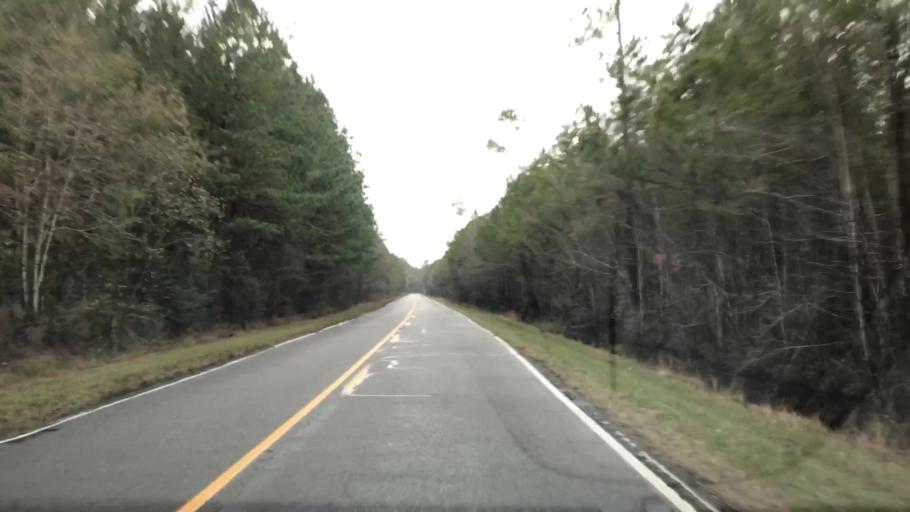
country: US
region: South Carolina
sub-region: Georgetown County
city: Murrells Inlet
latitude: 33.6320
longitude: -79.2508
